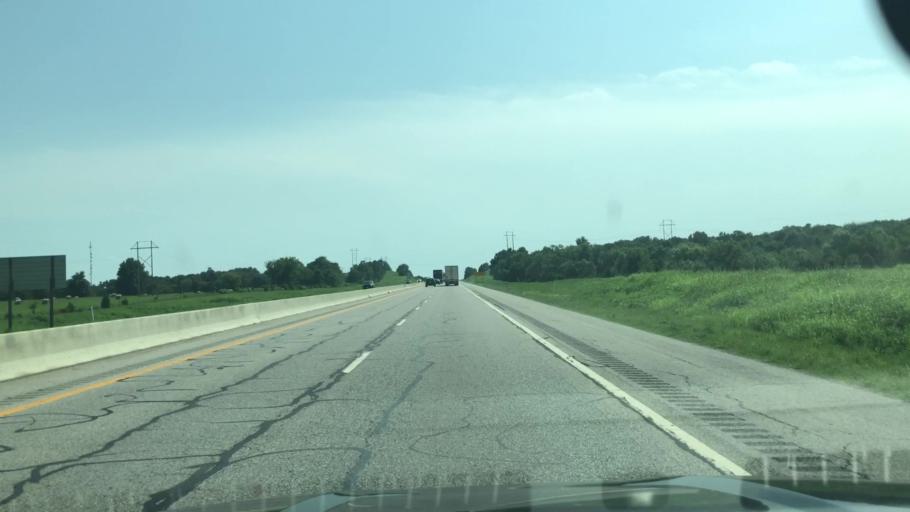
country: US
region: Oklahoma
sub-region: Ottawa County
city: Miami
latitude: 36.8419
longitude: -94.8609
